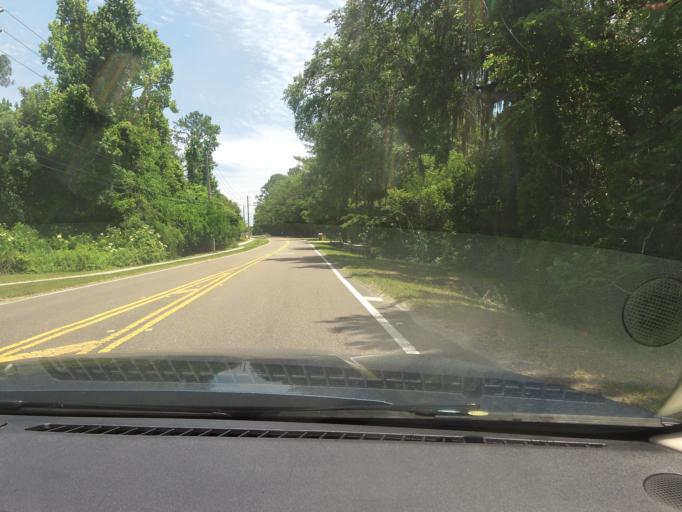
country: US
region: Florida
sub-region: Duval County
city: Jacksonville
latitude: 30.4686
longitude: -81.6159
